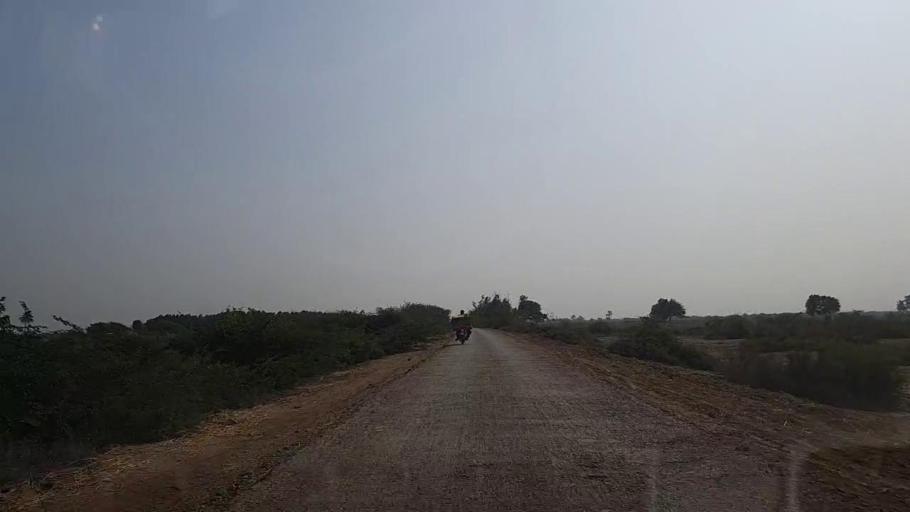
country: PK
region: Sindh
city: Keti Bandar
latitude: 24.2397
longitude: 67.6385
